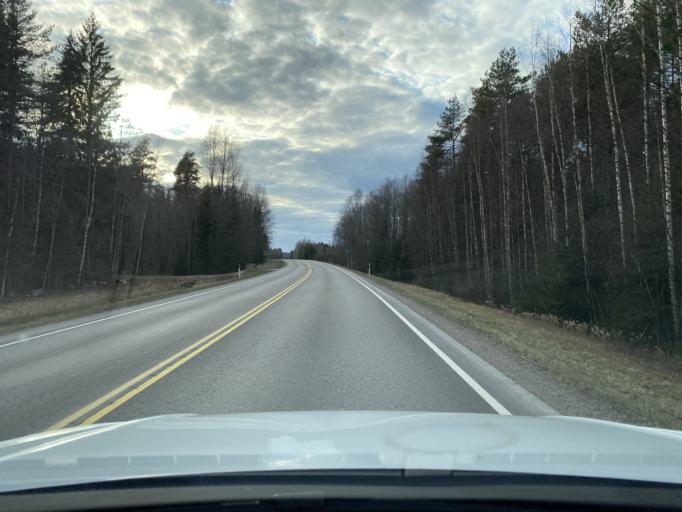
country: FI
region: Haeme
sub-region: Haemeenlinna
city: Renko
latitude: 60.7824
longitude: 24.1591
